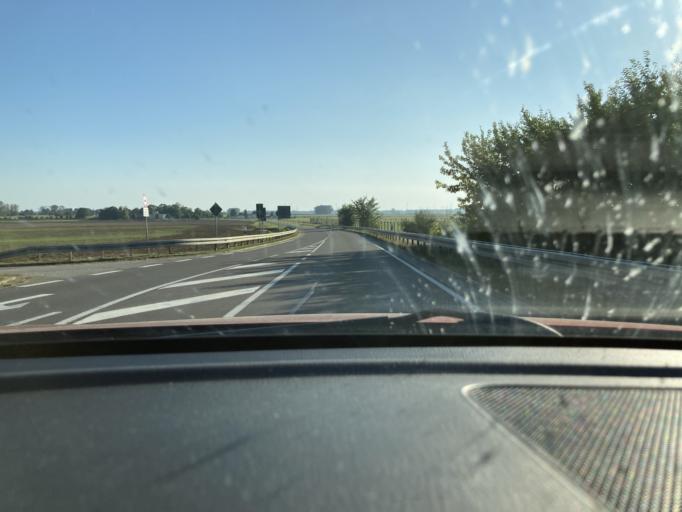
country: DE
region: Mecklenburg-Vorpommern
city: Anklam
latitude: 53.8350
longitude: 13.6811
